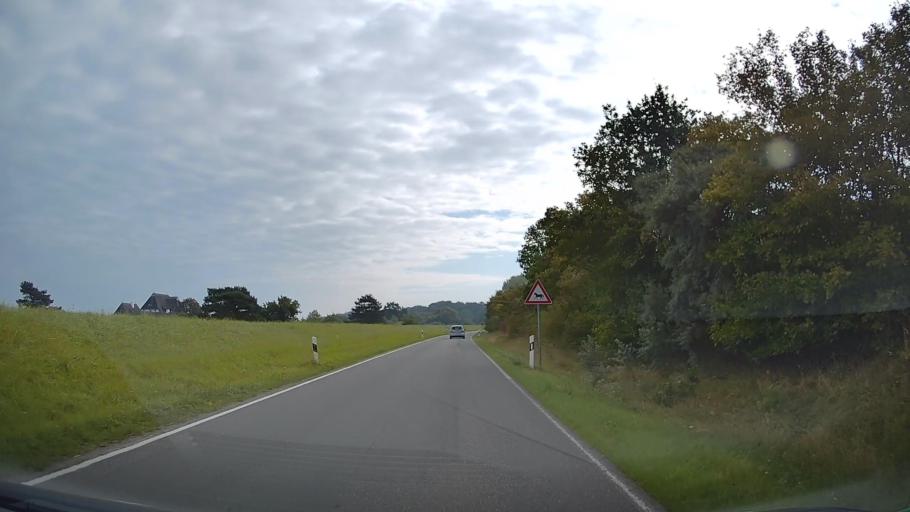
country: DE
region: Schleswig-Holstein
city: Blekendorf
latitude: 54.3280
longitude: 10.6551
